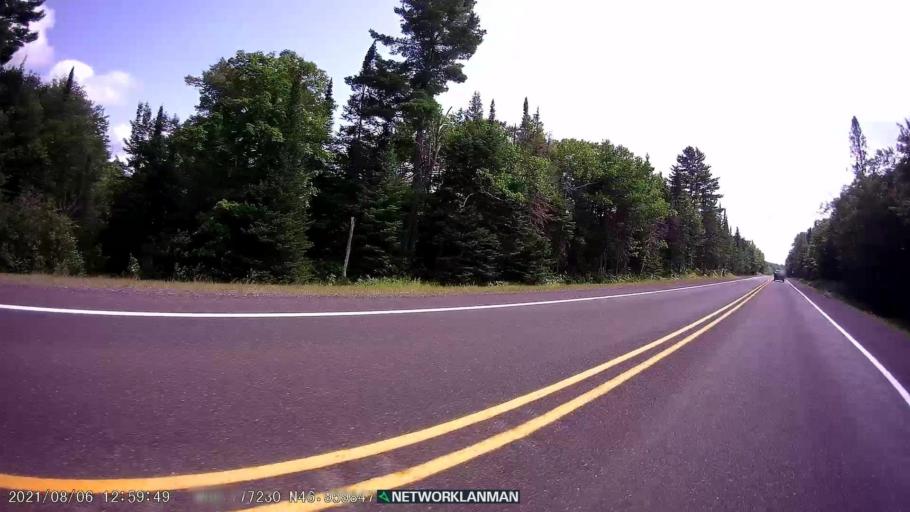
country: US
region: Michigan
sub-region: Houghton County
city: Hancock
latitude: 46.9595
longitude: -88.7774
